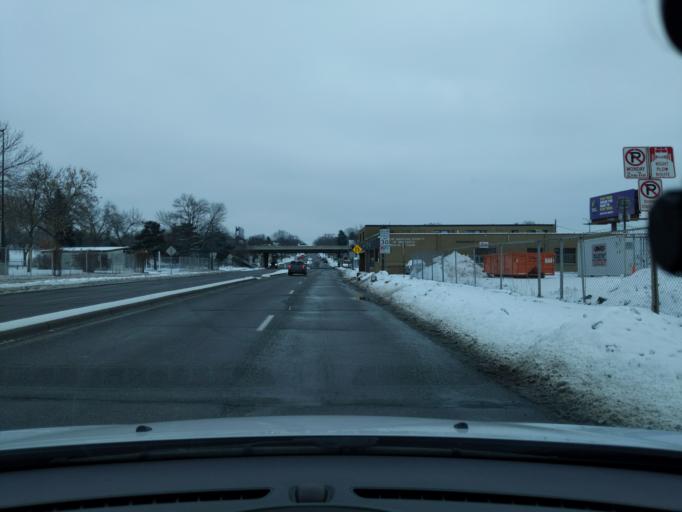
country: US
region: Minnesota
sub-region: Ramsey County
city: Falcon Heights
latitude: 44.9773
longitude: -93.1693
